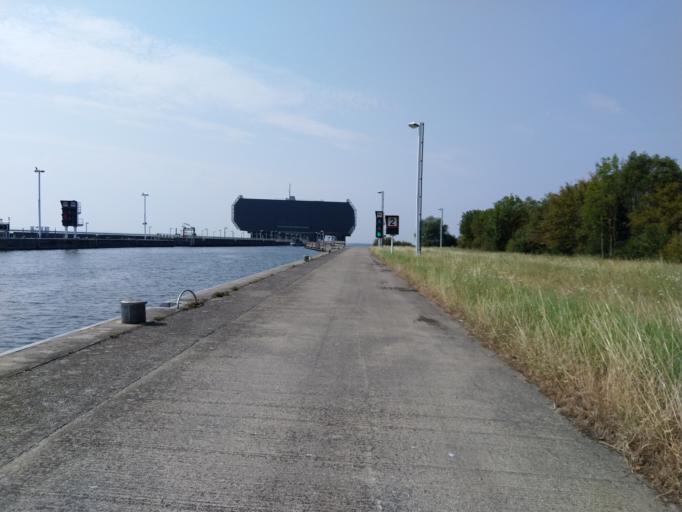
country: BE
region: Wallonia
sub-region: Province du Hainaut
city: Roeulx
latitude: 50.4819
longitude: 4.1124
